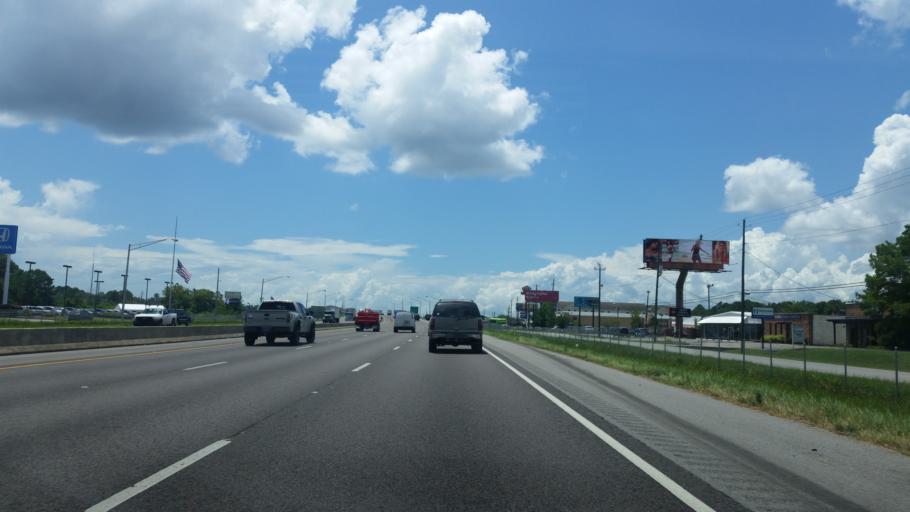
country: US
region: Alabama
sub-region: Mobile County
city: Prichard
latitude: 30.6666
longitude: -88.1273
